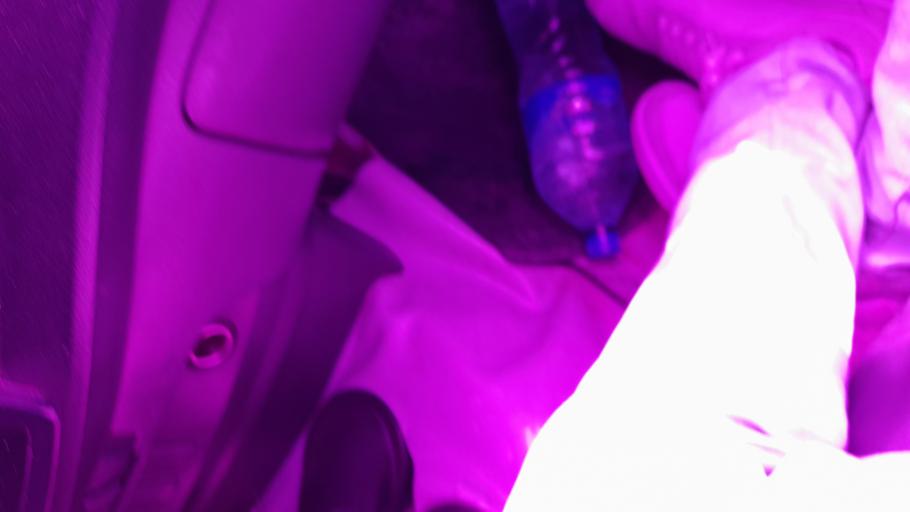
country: ET
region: Afar
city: Awash
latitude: 9.3634
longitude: 40.3066
